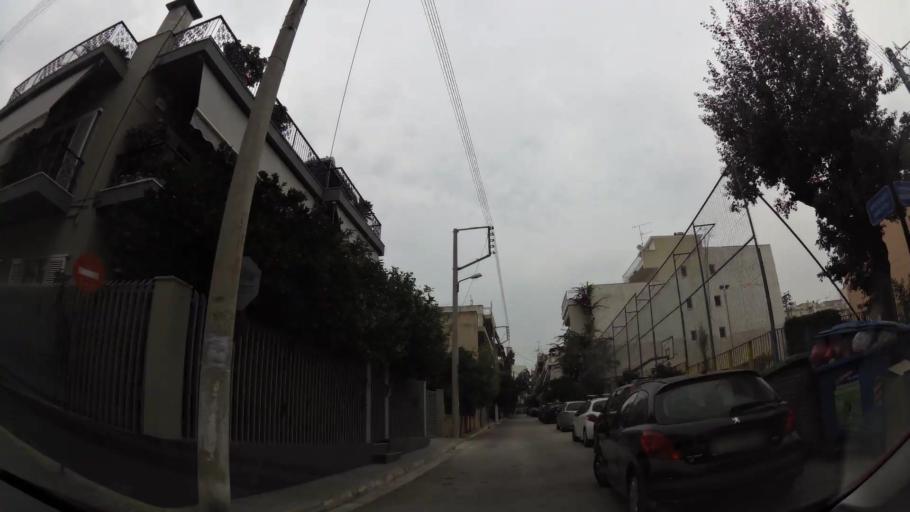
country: GR
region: Attica
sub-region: Nomarchia Athinas
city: Ilion
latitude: 38.0238
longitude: 23.7092
